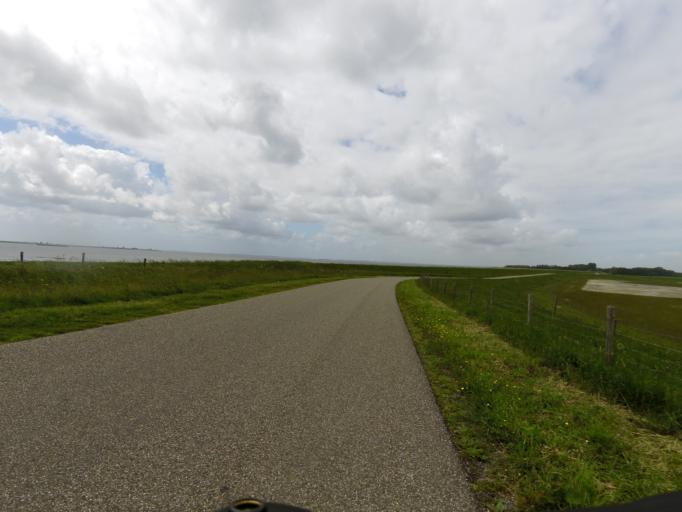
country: NL
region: Zeeland
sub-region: Schouwen-Duiveland
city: Bruinisse
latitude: 51.6179
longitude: 4.0033
